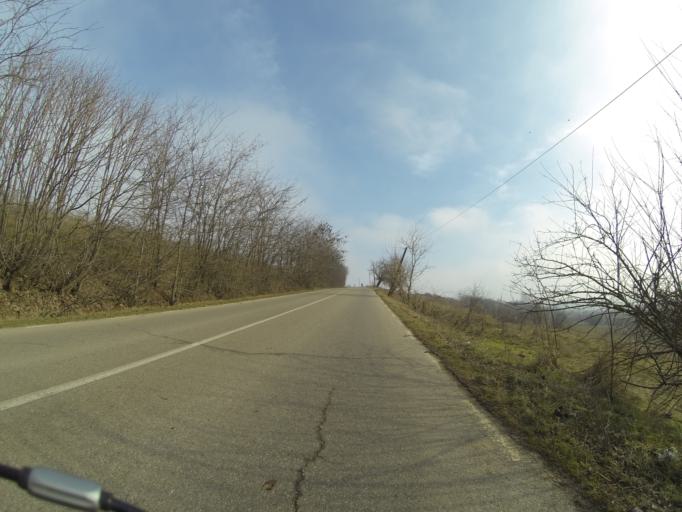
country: RO
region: Mehedinti
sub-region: Comuna Balacita
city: Balacita
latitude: 44.3869
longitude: 23.1334
